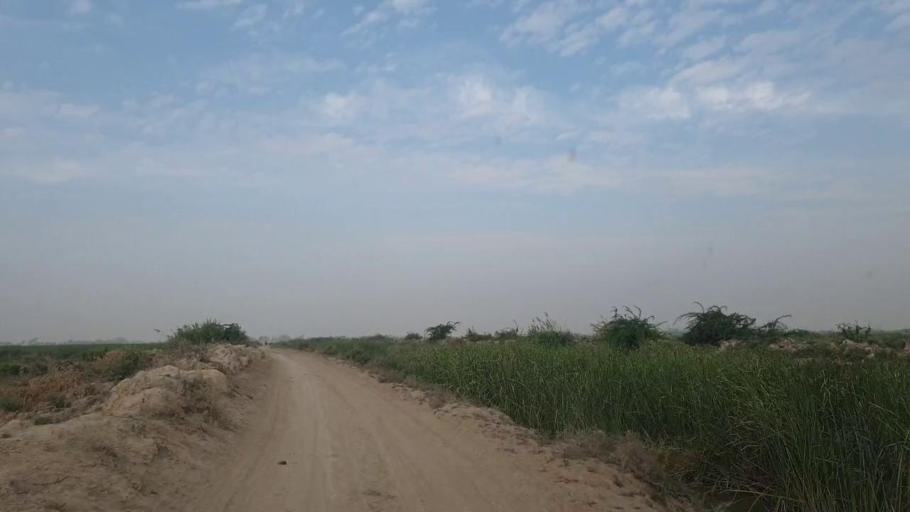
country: PK
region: Sindh
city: Tando Bago
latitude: 24.8670
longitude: 68.9837
